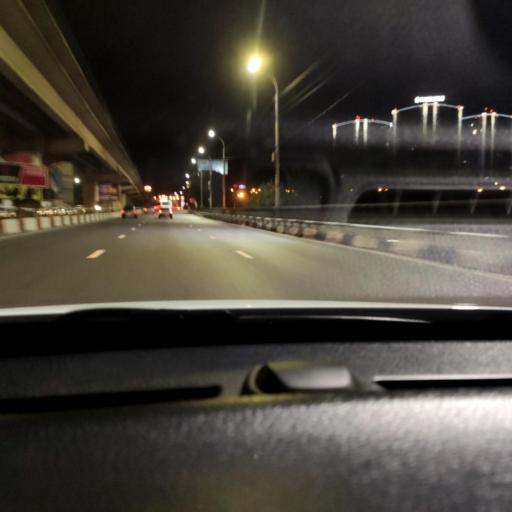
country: RU
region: Voronezj
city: Voronezh
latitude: 51.6933
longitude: 39.2346
